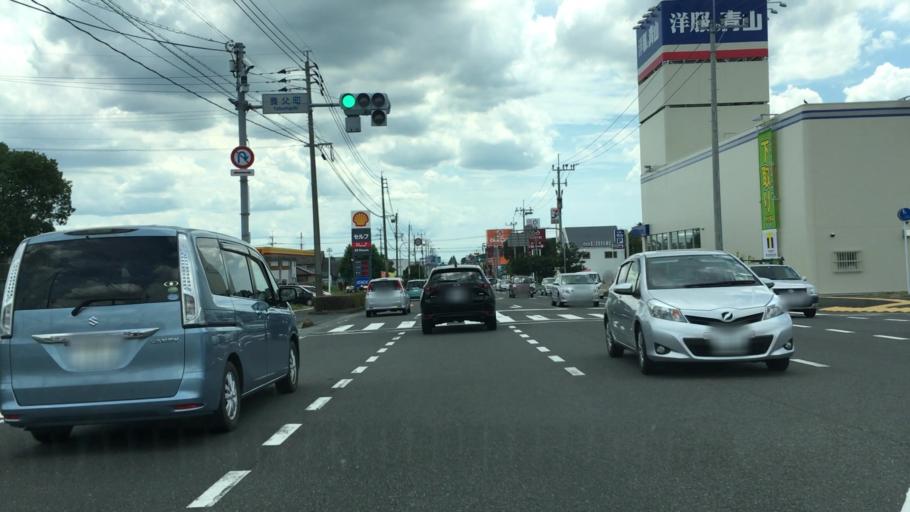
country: JP
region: Saga Prefecture
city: Tosu
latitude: 33.3799
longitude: 130.4990
